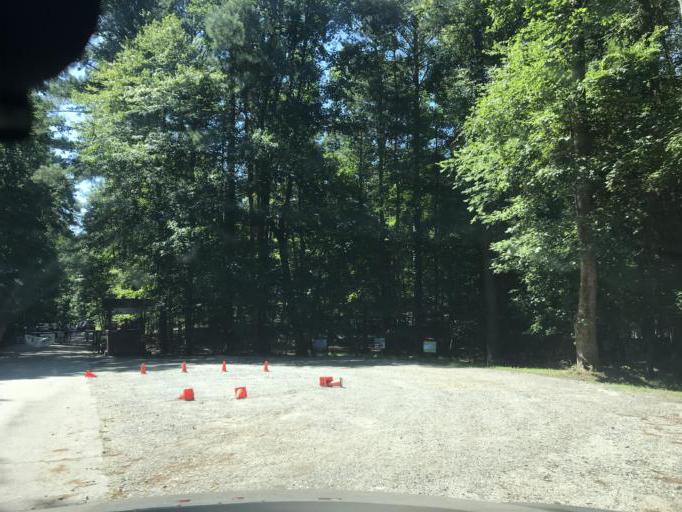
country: US
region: Georgia
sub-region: Forsyth County
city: Cumming
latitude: 34.1990
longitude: -84.1094
